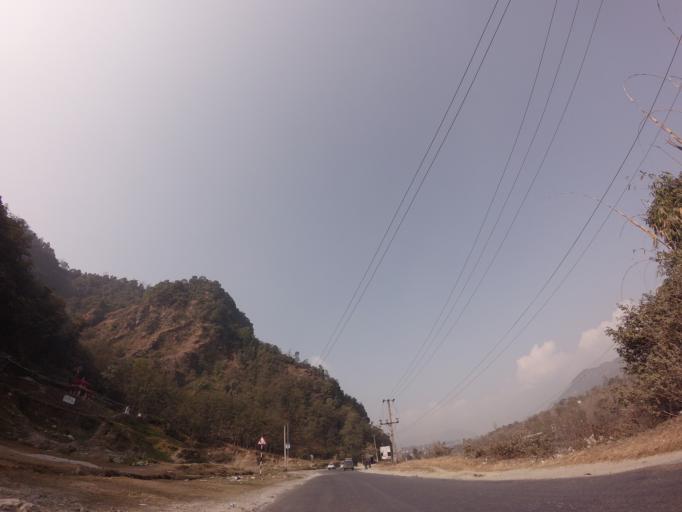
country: NP
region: Western Region
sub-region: Gandaki Zone
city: Pokhara
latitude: 28.2486
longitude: 83.9745
